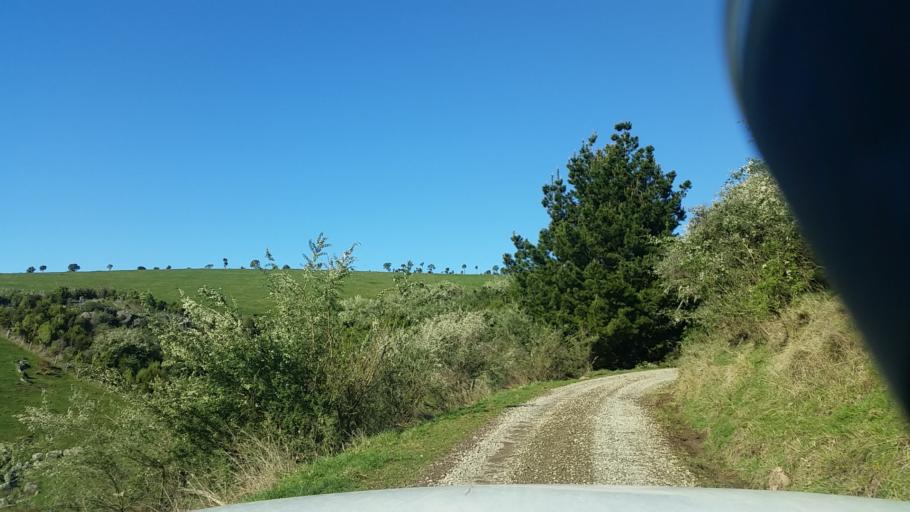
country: NZ
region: Canterbury
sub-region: Christchurch City
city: Christchurch
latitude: -43.6510
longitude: 172.9683
